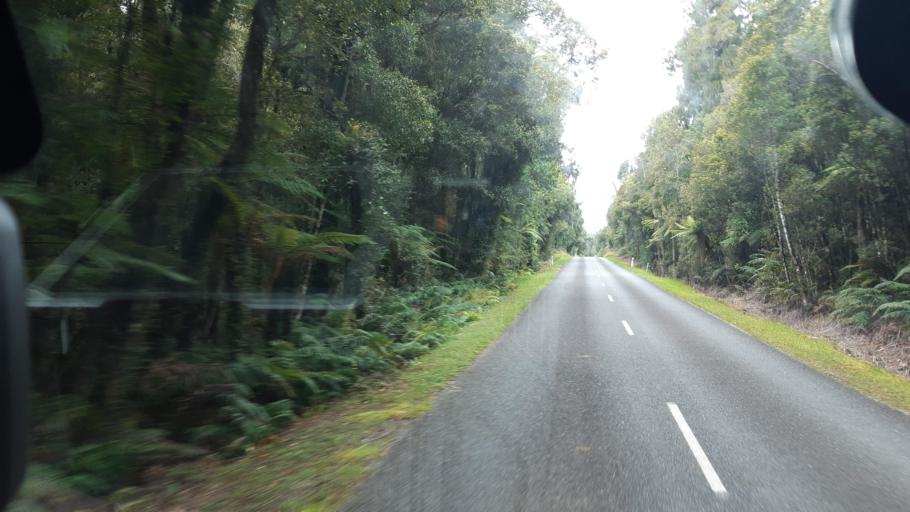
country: NZ
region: West Coast
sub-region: Westland District
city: Hokitika
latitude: -42.7818
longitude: 171.1105
